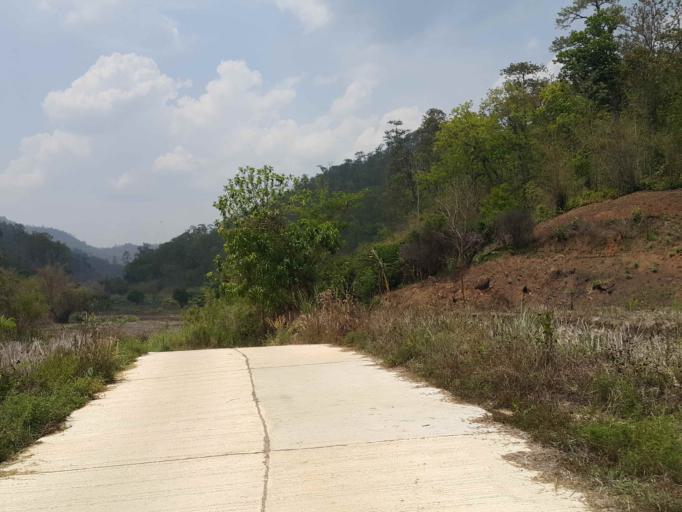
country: TH
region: Chiang Mai
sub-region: Amphoe Chiang Dao
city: Chiang Dao
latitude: 19.2735
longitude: 98.7664
